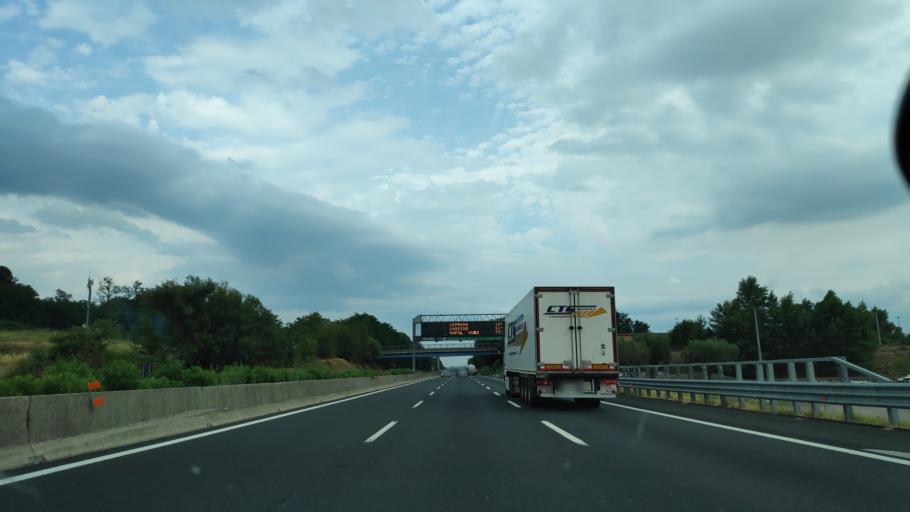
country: IT
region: Latium
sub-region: Provincia di Frosinone
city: Frosinone
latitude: 41.6272
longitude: 13.2907
